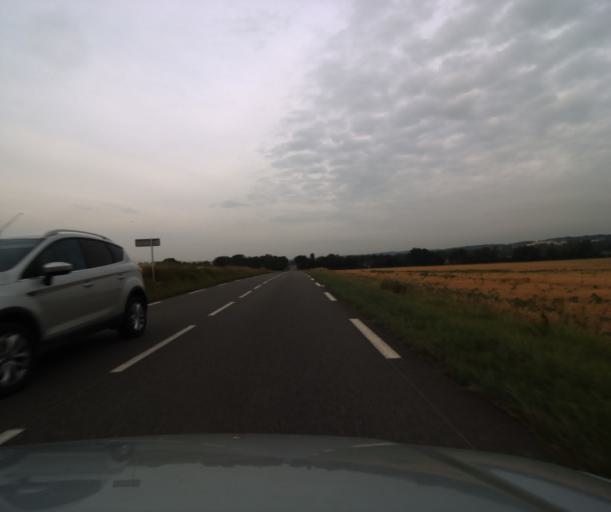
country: FR
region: Midi-Pyrenees
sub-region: Departement du Gers
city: Aubiet
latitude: 43.6701
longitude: 0.8031
